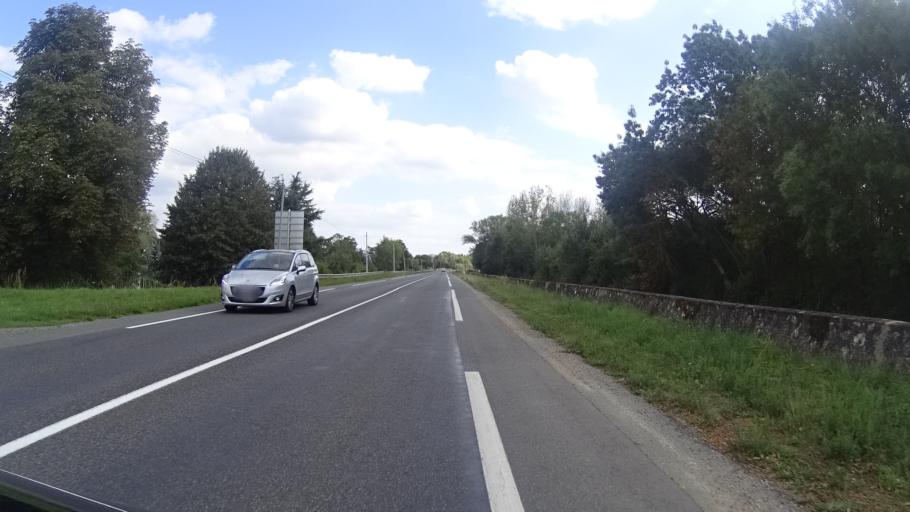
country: FR
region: Pays de la Loire
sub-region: Departement de Maine-et-Loire
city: Saint-Martin-de-la-Place
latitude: 47.3050
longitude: -0.1308
